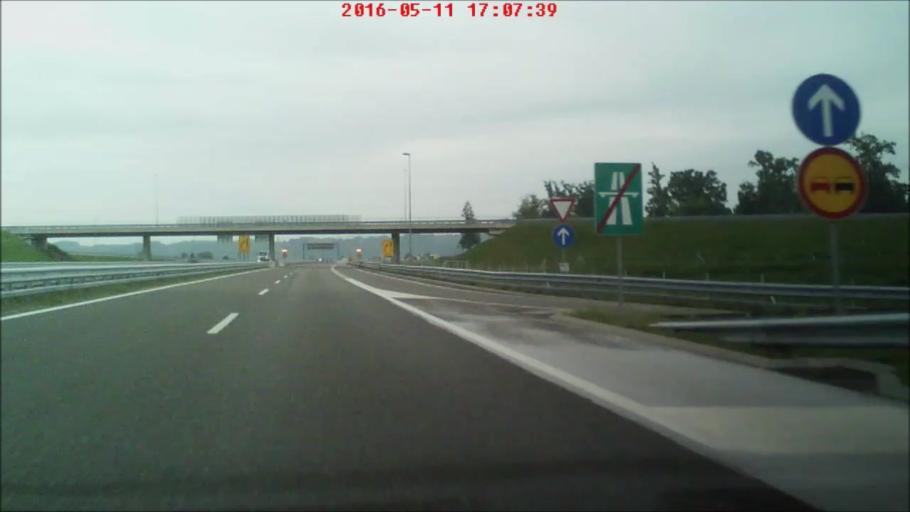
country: SI
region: Hajdina
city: Spodnja Hajdina
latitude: 46.3925
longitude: 15.8561
